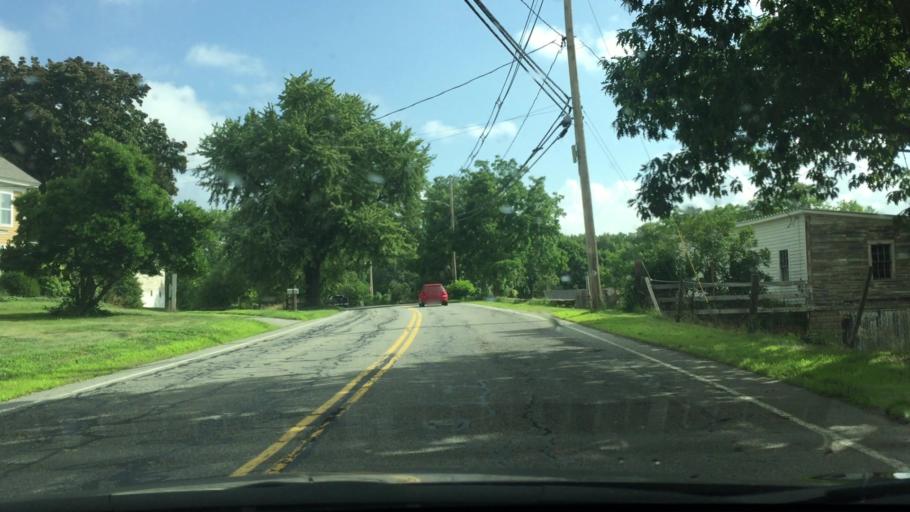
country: US
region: Massachusetts
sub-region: Middlesex County
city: Littleton Common
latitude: 42.5238
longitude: -71.4601
